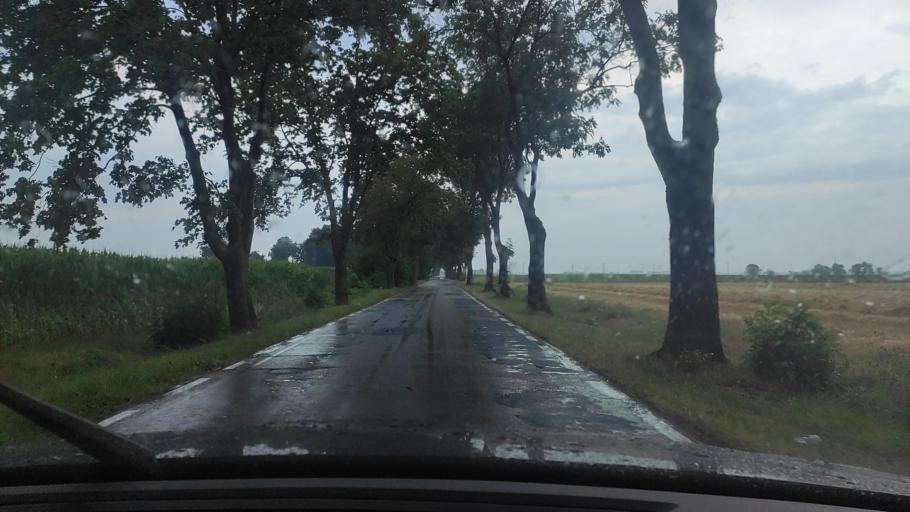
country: PL
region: Greater Poland Voivodeship
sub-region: Powiat poznanski
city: Kleszczewo
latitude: 52.2895
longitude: 17.1884
